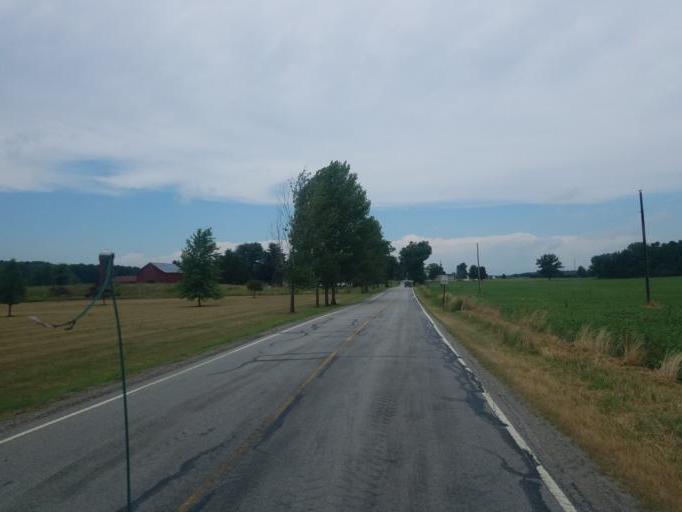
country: US
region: Indiana
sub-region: DeKalb County
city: Butler
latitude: 41.3861
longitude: -84.8506
